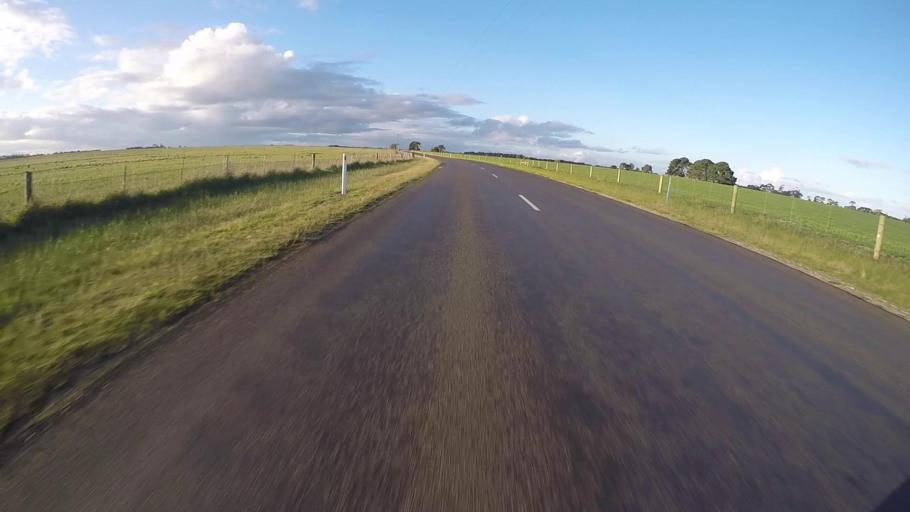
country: AU
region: Victoria
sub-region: Greater Geelong
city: Wandana Heights
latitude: -38.1382
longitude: 144.1970
